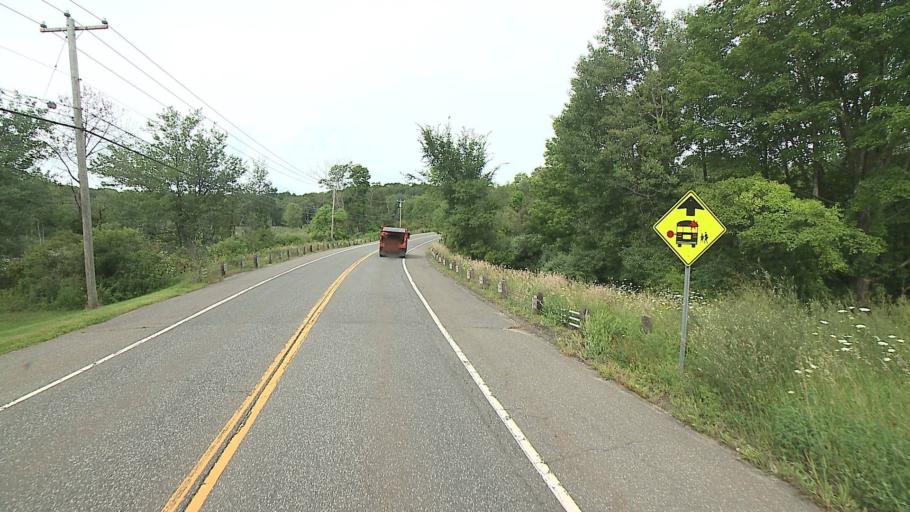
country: US
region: Connecticut
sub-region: Litchfield County
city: New Preston
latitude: 41.7420
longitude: -73.3866
